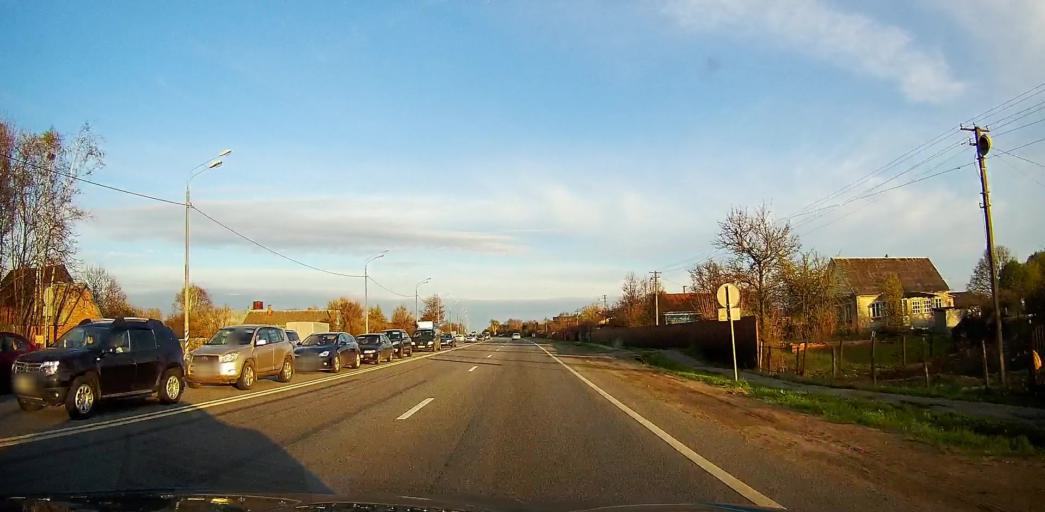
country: RU
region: Moskovskaya
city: Troitskoye
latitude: 55.2465
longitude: 38.5301
